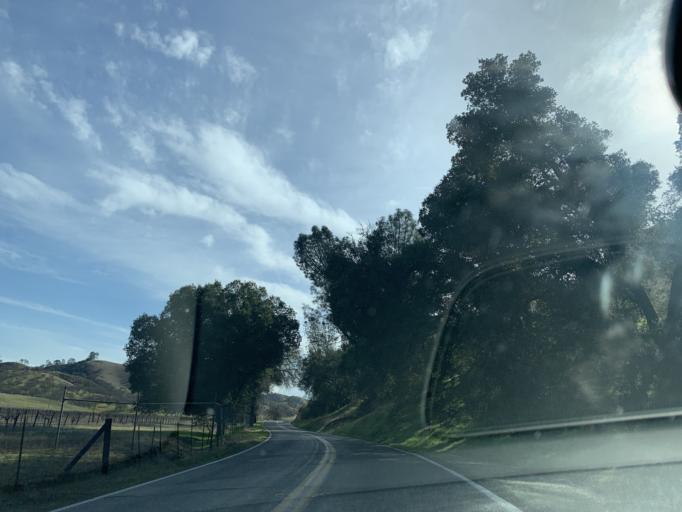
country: US
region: California
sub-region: Monterey County
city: Soledad
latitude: 36.5155
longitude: -121.1236
